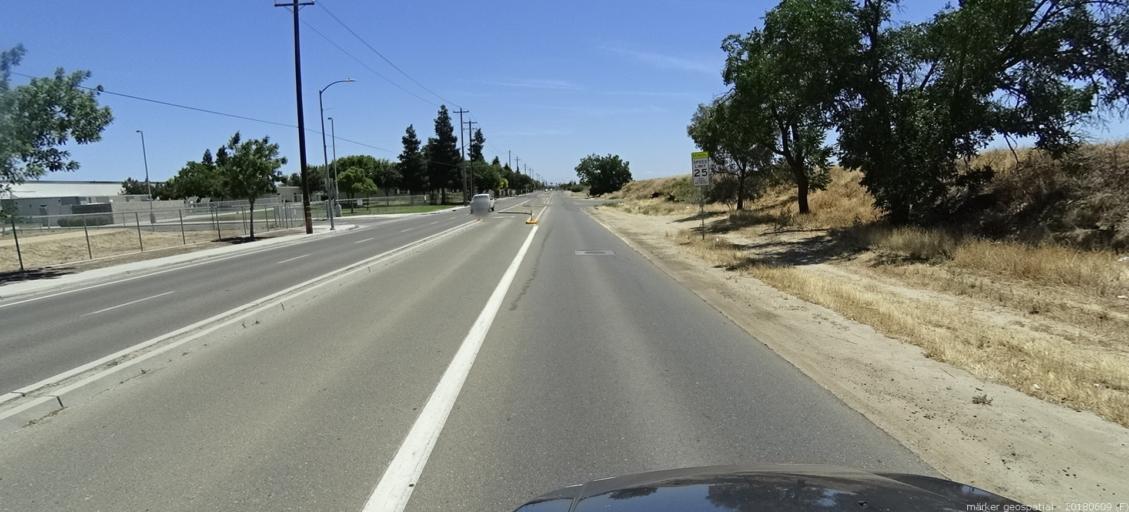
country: US
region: California
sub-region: Madera County
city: Madera
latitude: 36.9383
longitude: -120.0706
